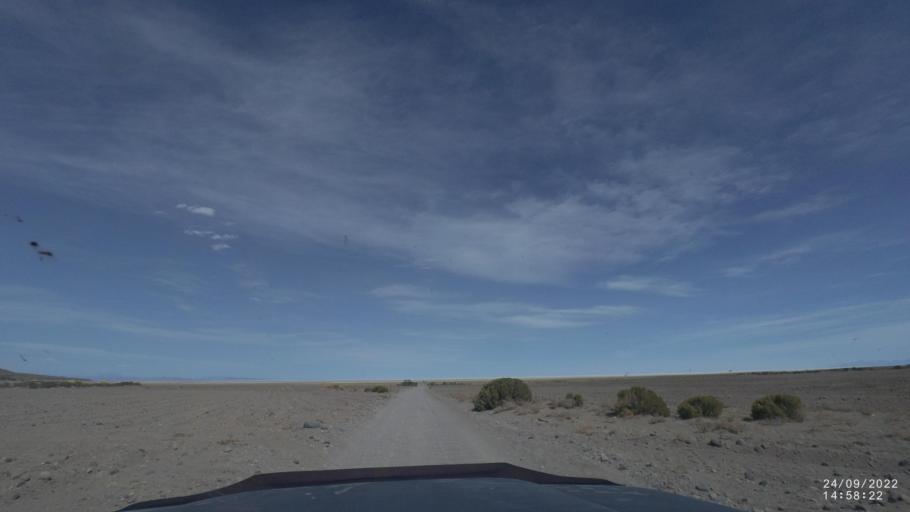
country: BO
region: Potosi
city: Colchani
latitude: -19.8605
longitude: -67.5683
